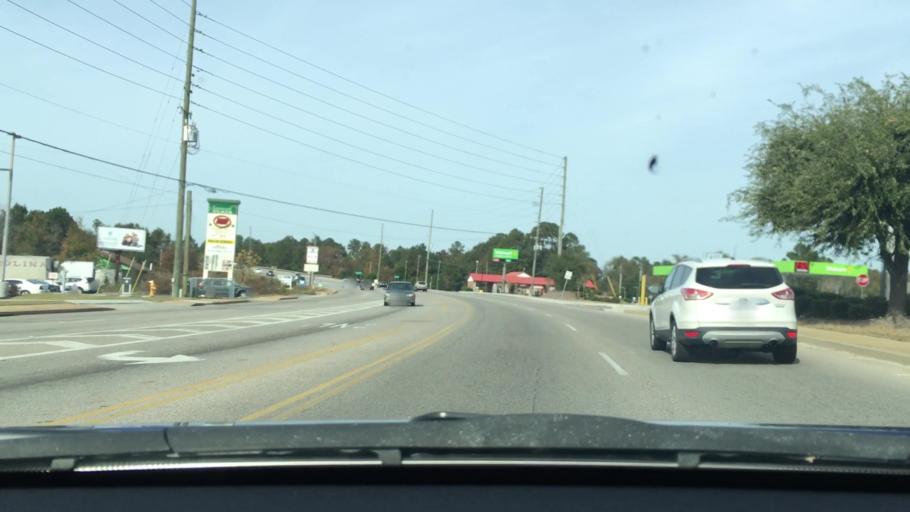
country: US
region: South Carolina
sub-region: Sumter County
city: South Sumter
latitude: 33.9047
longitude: -80.3792
